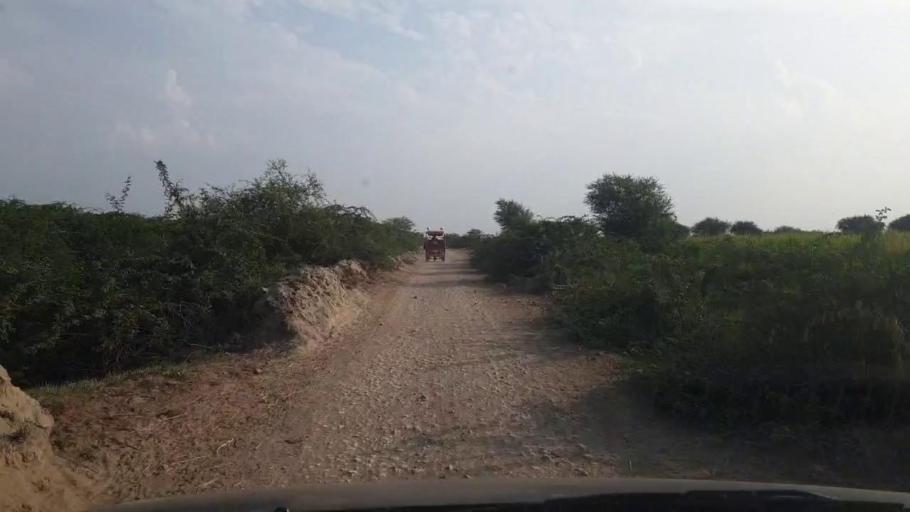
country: PK
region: Sindh
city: Badin
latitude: 24.5664
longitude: 68.6672
